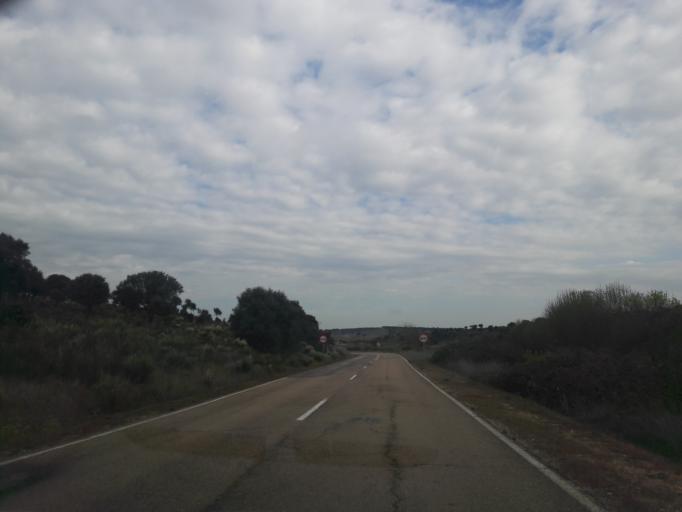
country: ES
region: Castille and Leon
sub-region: Provincia de Salamanca
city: Pastores
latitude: 40.5340
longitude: -6.5258
